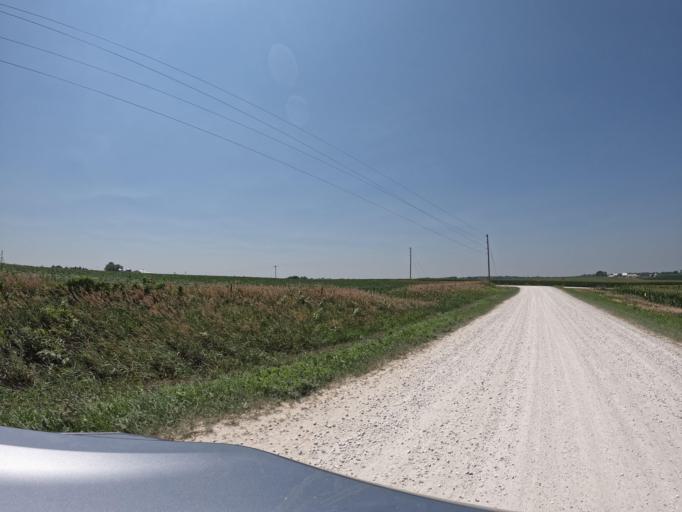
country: US
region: Iowa
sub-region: Keokuk County
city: Sigourney
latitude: 41.2866
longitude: -92.2178
